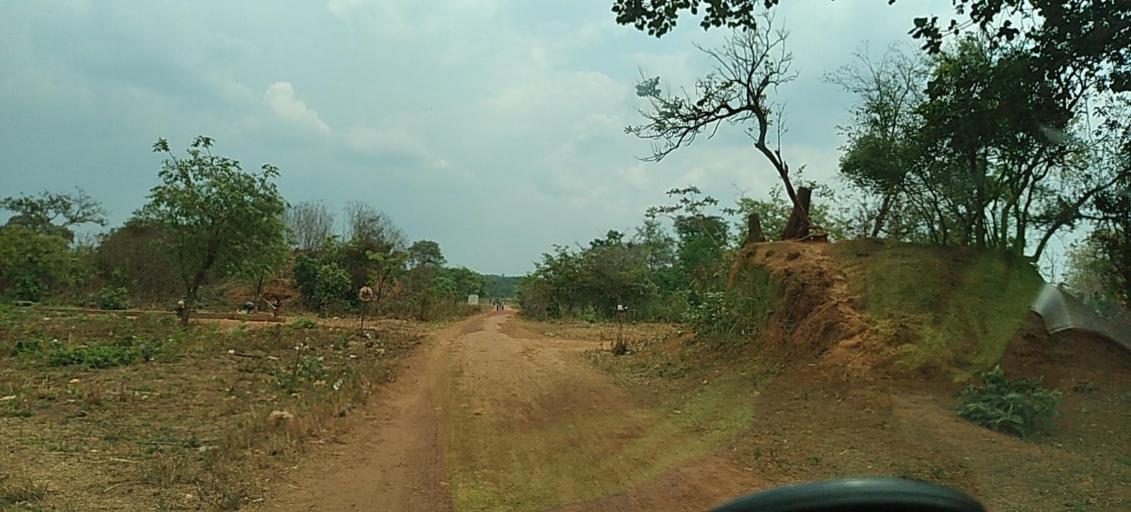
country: ZM
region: North-Western
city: Kansanshi
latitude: -11.9920
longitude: 26.2842
